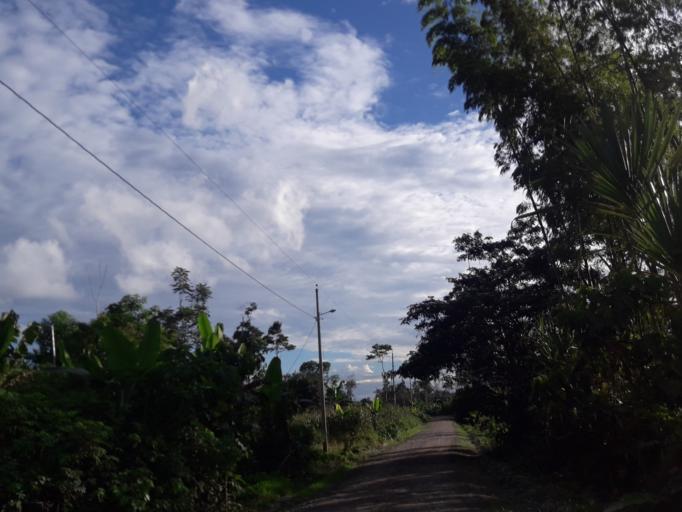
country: EC
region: Orellana
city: Boca Suno
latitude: -0.8848
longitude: -77.2970
